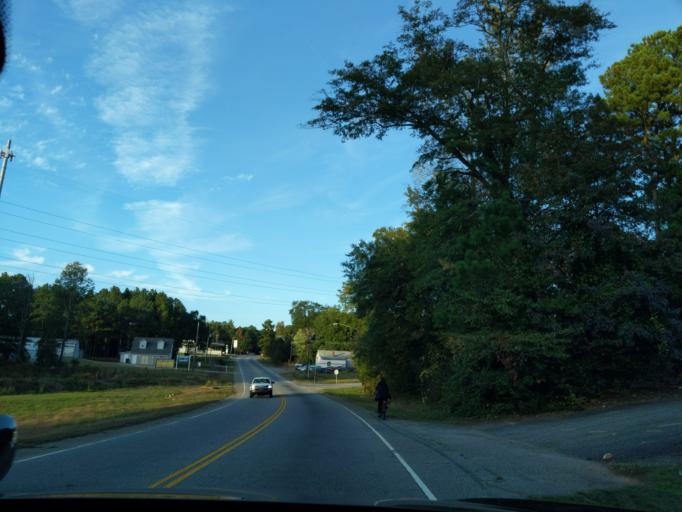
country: US
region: South Carolina
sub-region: Anderson County
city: Anderson
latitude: 34.5027
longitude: -82.6075
